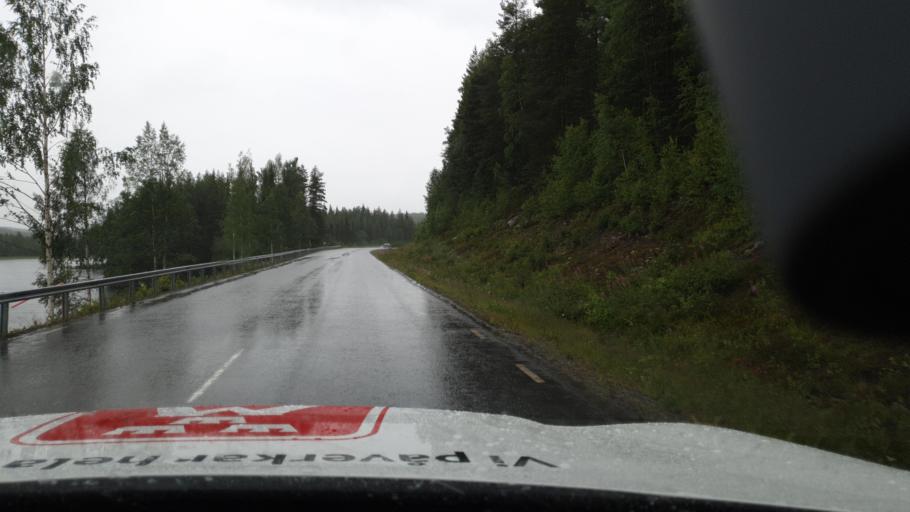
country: SE
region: Vaesterbotten
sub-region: Norsjo Kommun
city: Norsjoe
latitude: 64.8468
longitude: 19.7520
